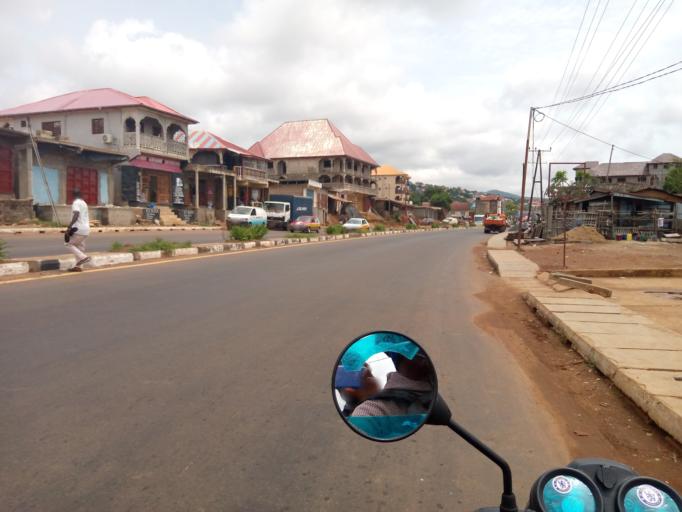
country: SL
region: Western Area
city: Hastings
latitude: 8.4140
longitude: -13.1497
